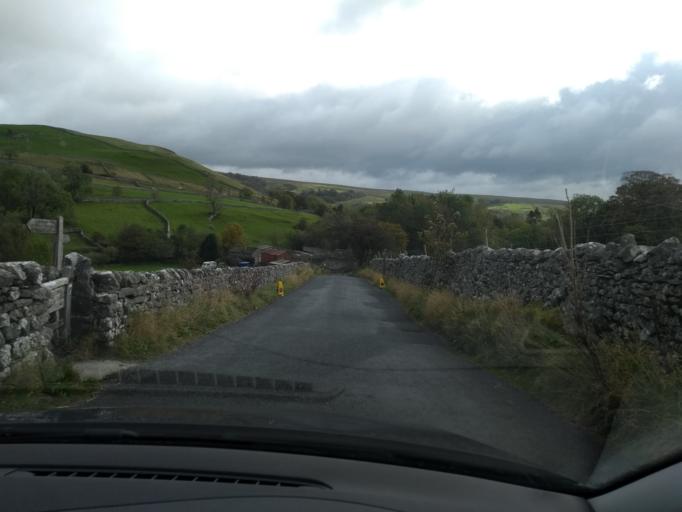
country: GB
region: England
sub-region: North Yorkshire
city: Gargrave
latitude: 54.0657
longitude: -2.1577
